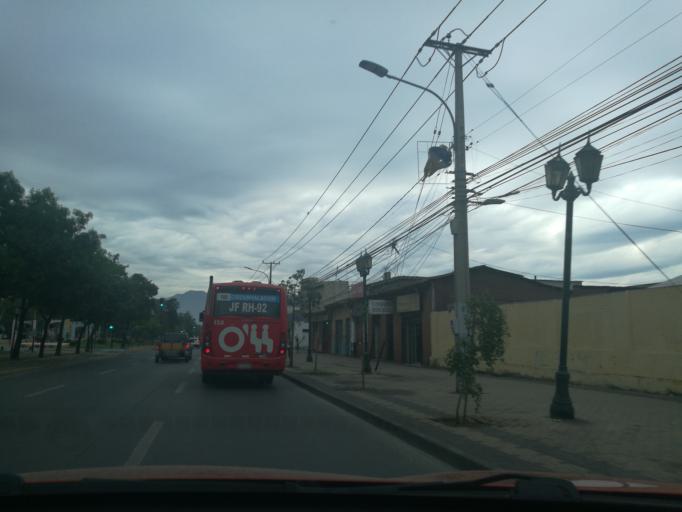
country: CL
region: O'Higgins
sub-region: Provincia de Cachapoal
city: Rancagua
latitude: -34.1656
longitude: -70.7377
